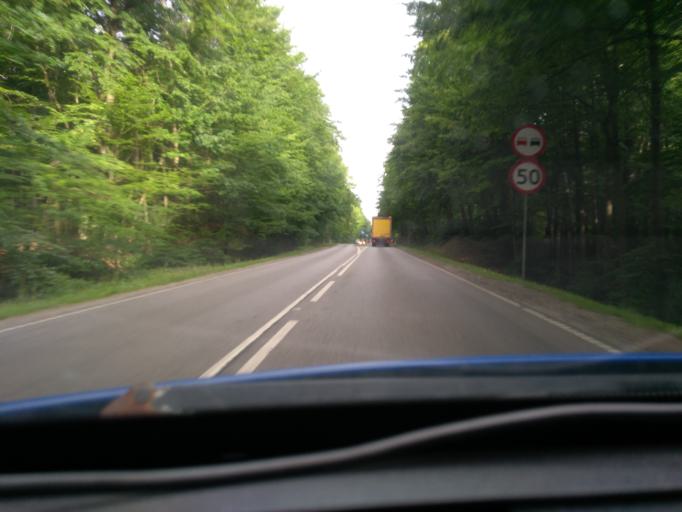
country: PL
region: Pomeranian Voivodeship
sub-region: Powiat kartuski
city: Kartuzy
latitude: 54.3275
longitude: 18.2257
